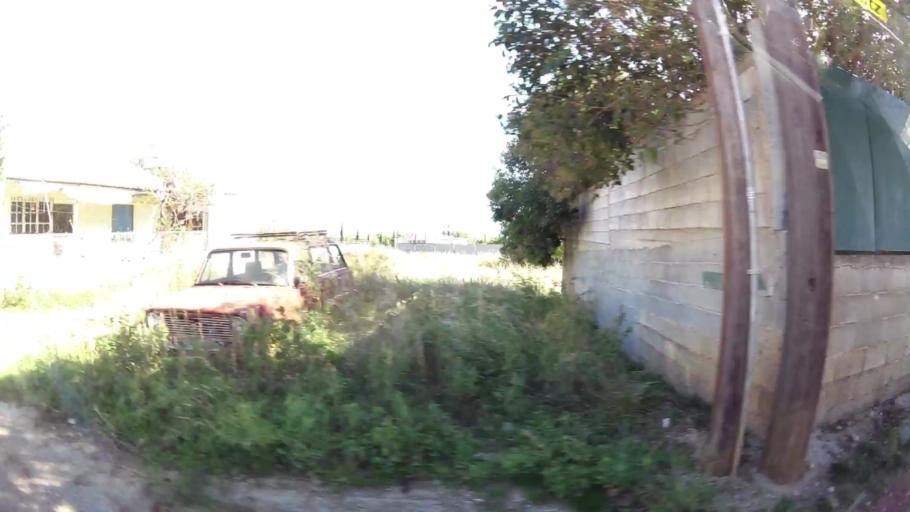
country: GR
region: Attica
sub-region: Nomarchia Anatolikis Attikis
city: Acharnes
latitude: 38.1069
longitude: 23.7222
